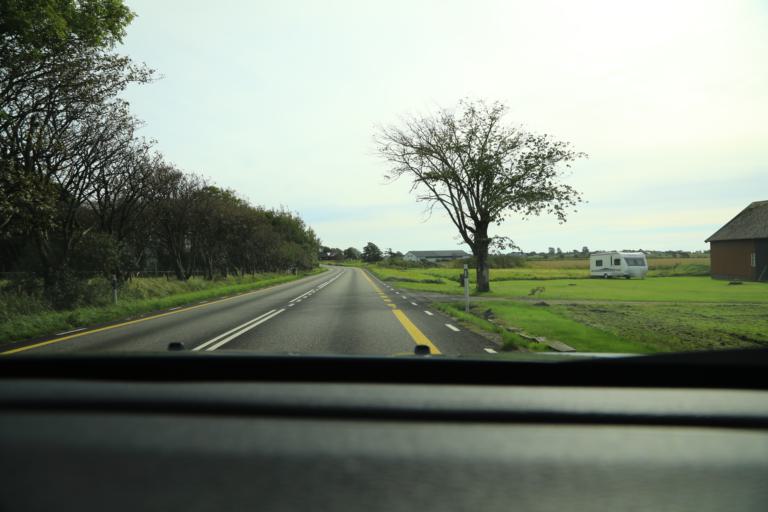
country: SE
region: Halland
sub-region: Varbergs Kommun
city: Traslovslage
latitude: 57.0390
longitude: 12.3236
